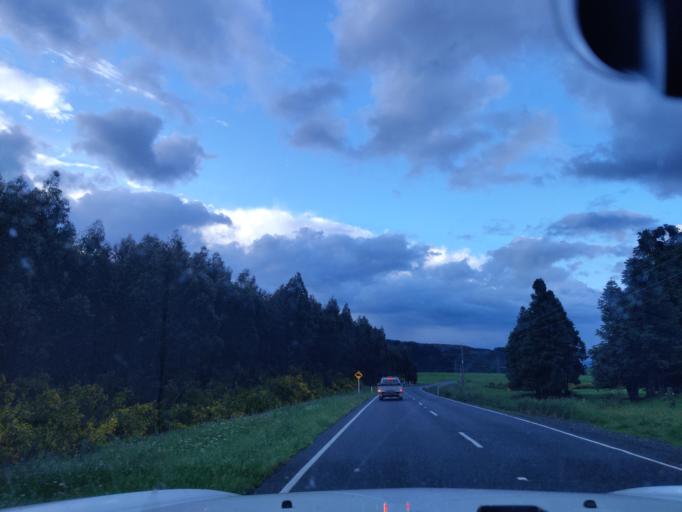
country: NZ
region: Waikato
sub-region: South Waikato District
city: Tokoroa
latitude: -38.3629
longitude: 175.8066
